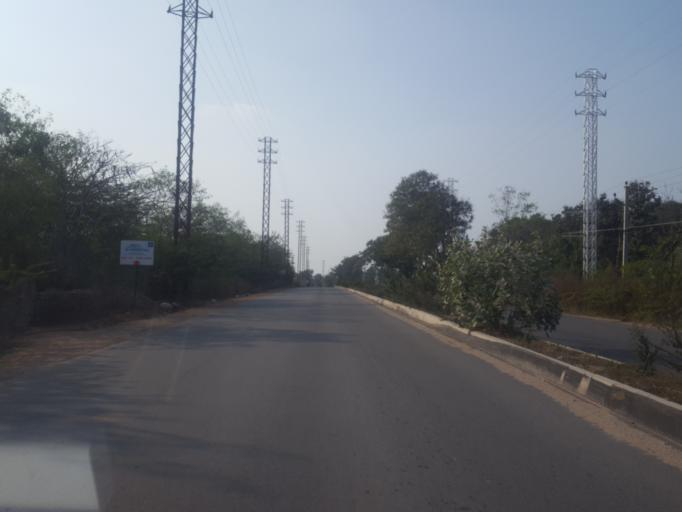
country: IN
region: Telangana
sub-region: Medak
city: Serilingampalle
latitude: 17.4149
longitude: 78.2616
